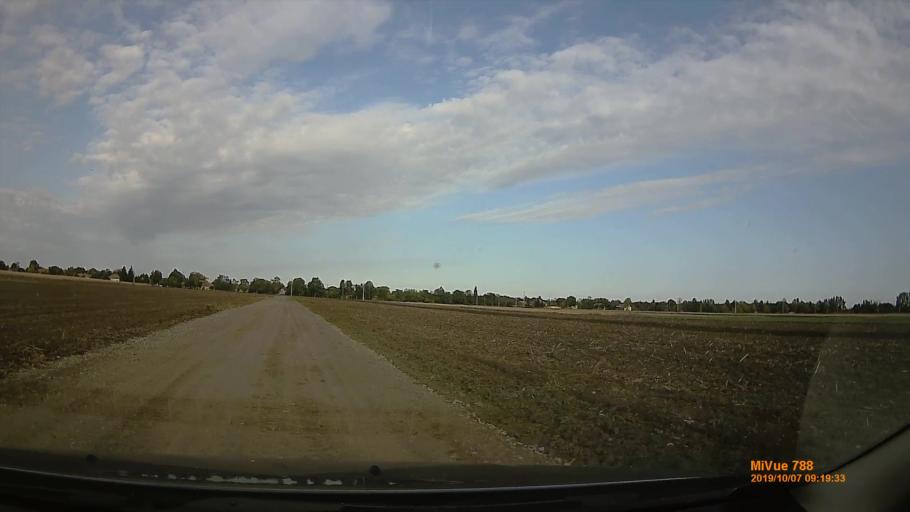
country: HU
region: Bekes
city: Szarvas
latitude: 46.8166
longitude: 20.6610
